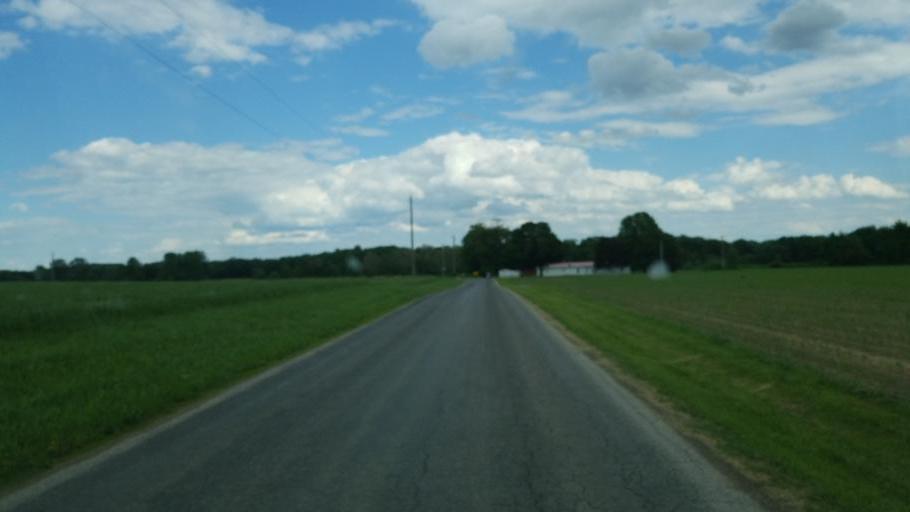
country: US
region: Ohio
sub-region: Huron County
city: Plymouth
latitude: 40.9452
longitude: -82.6215
